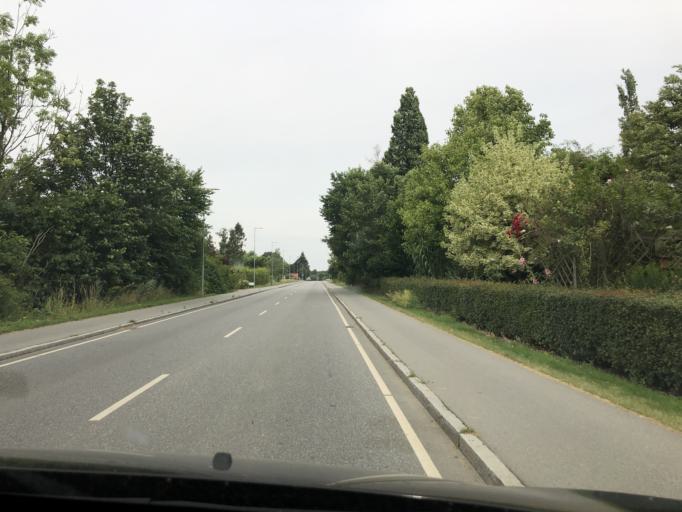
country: DK
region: South Denmark
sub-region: Assens Kommune
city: Glamsbjerg
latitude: 55.2575
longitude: 10.1322
